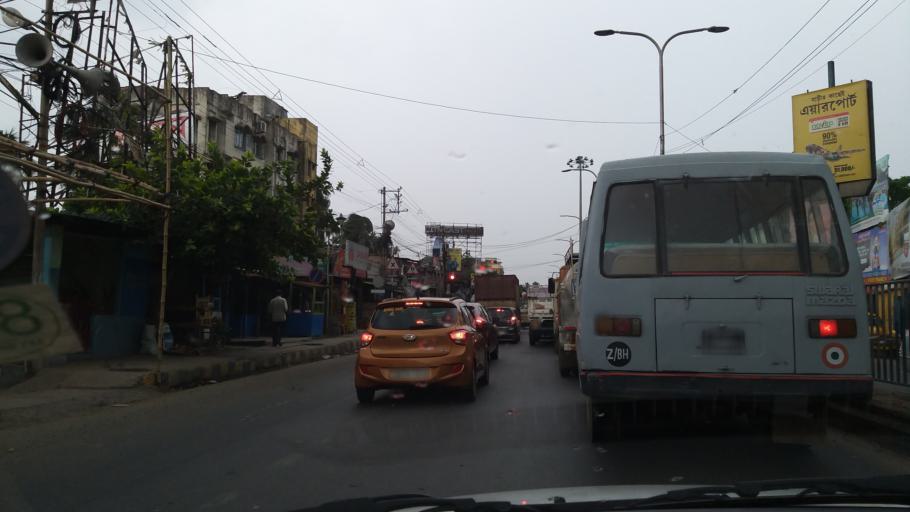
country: IN
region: West Bengal
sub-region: North 24 Parganas
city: Madhyamgram
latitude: 22.6587
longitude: 88.4412
